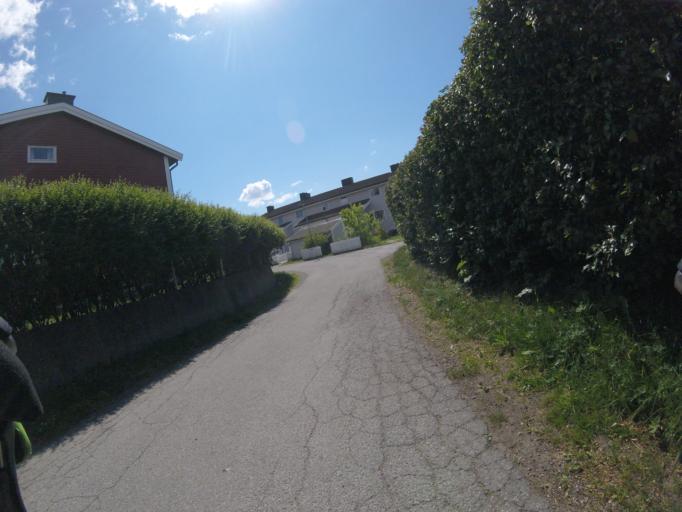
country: NO
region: Akershus
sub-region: Skedsmo
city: Lillestrom
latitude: 59.9526
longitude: 11.0563
